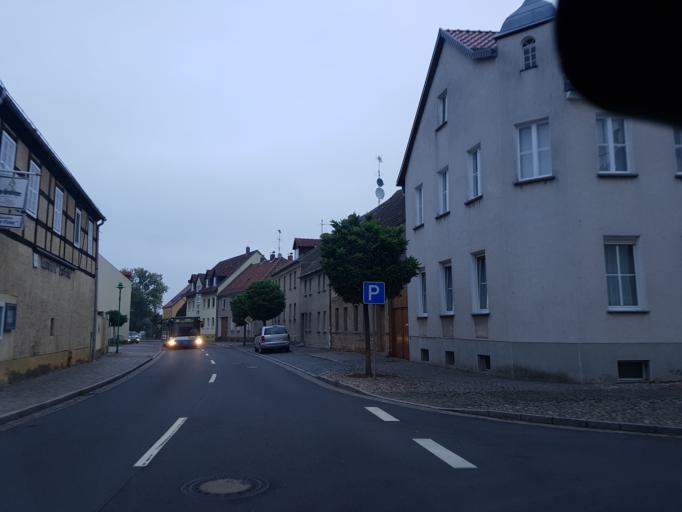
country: DE
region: Saxony-Anhalt
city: Annaburg
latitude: 51.7929
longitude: 13.0251
